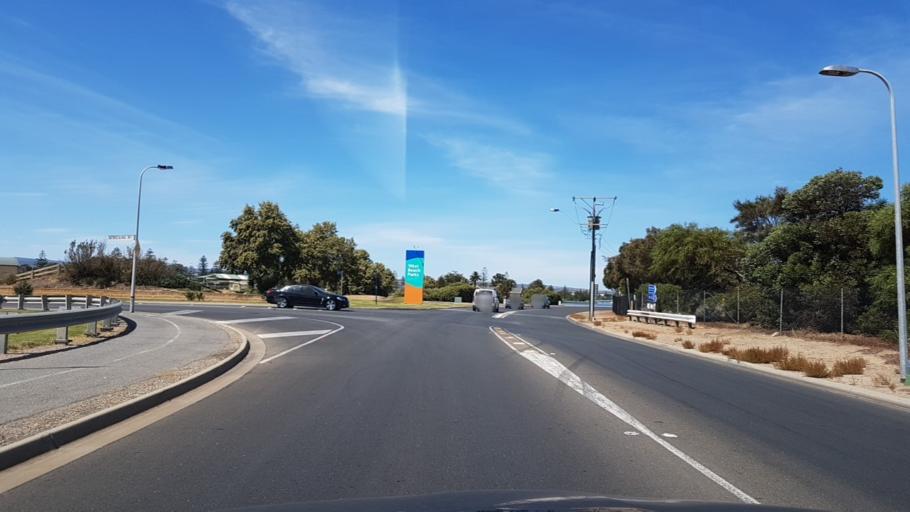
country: AU
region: South Australia
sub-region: Adelaide
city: Glenelg
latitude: -34.9605
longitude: 138.5123
